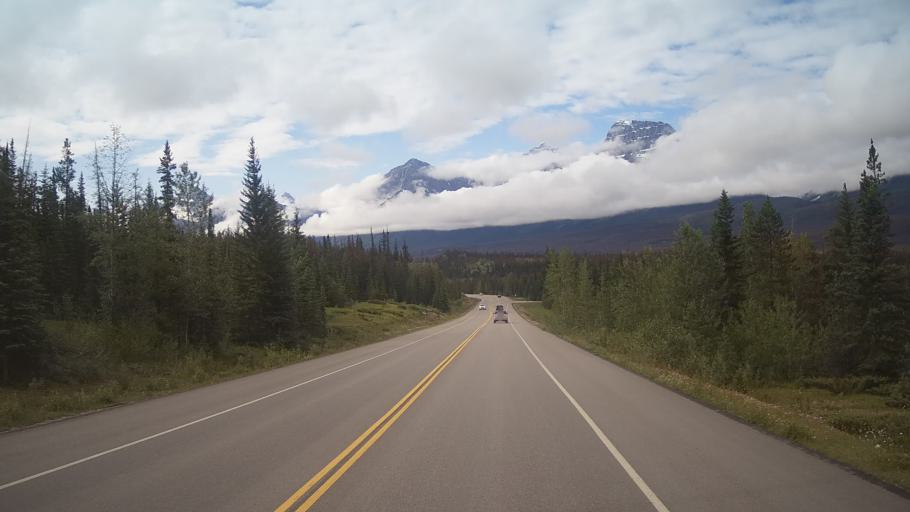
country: CA
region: Alberta
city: Jasper Park Lodge
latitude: 52.6720
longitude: -117.8813
